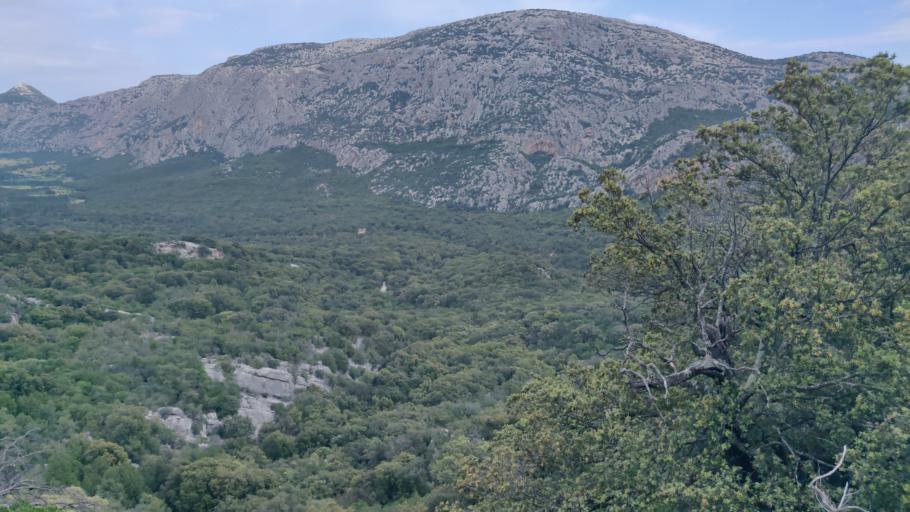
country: IT
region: Sardinia
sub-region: Provincia di Nuoro
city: Oliena
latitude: 40.2479
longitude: 9.4819
